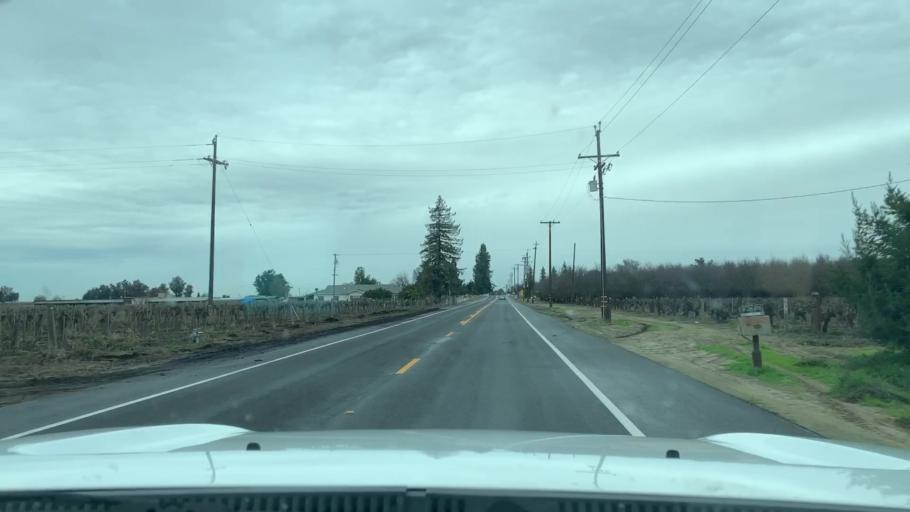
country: US
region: California
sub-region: Fresno County
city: Fowler
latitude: 36.5677
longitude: -119.6825
